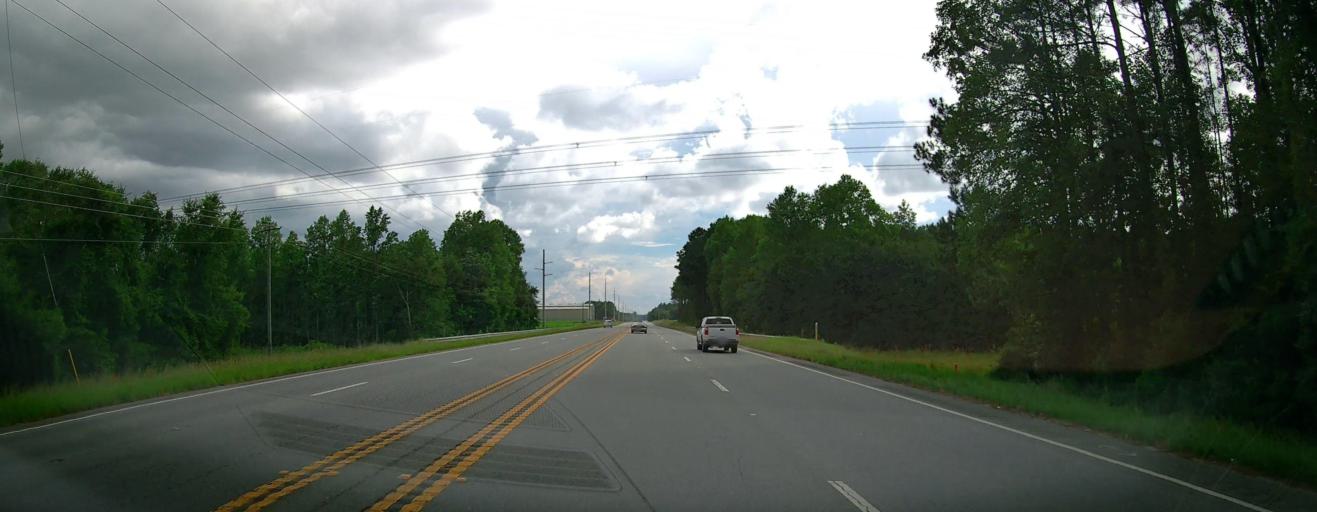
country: US
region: Georgia
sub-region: Pierce County
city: Blackshear
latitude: 31.4043
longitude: -82.1186
